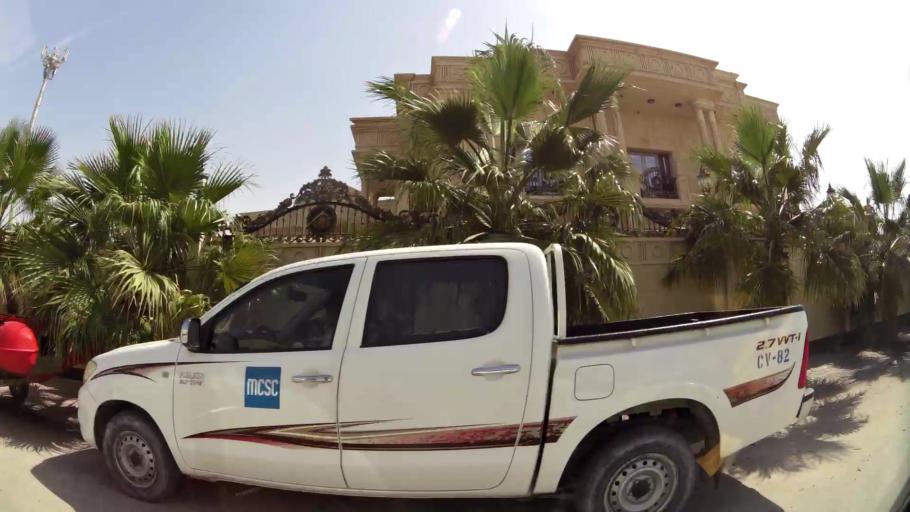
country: BH
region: Northern
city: Madinat `Isa
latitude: 26.1937
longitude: 50.4605
